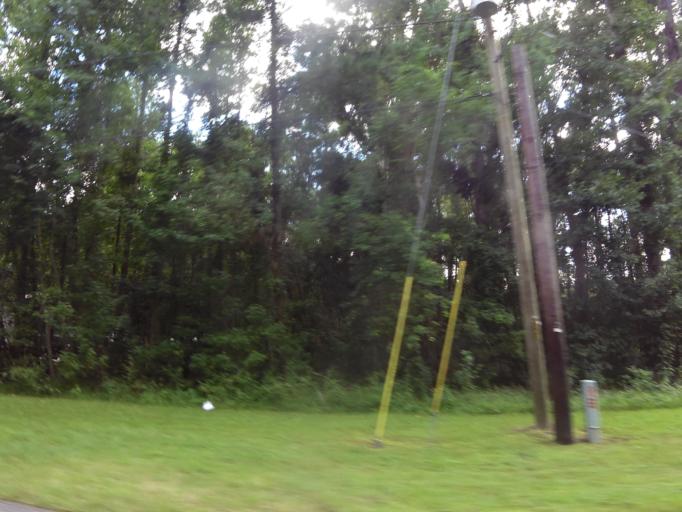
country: US
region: Georgia
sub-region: Camden County
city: Kingsland
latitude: 30.8035
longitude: -81.6938
